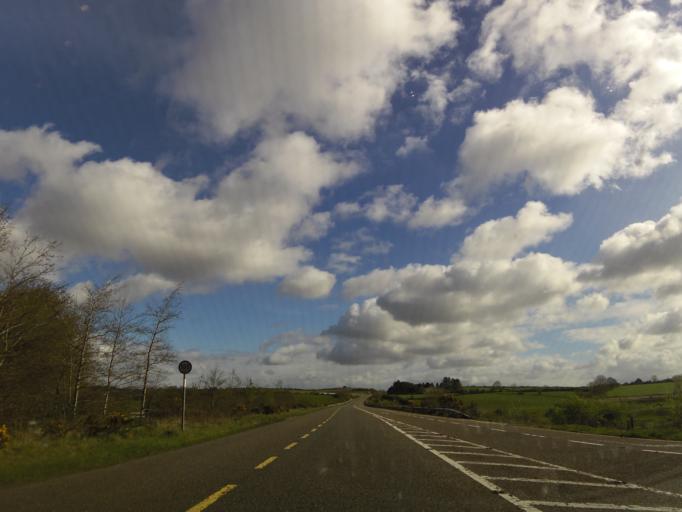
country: IE
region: Connaught
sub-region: Maigh Eo
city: Claremorris
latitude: 53.7796
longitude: -8.9479
